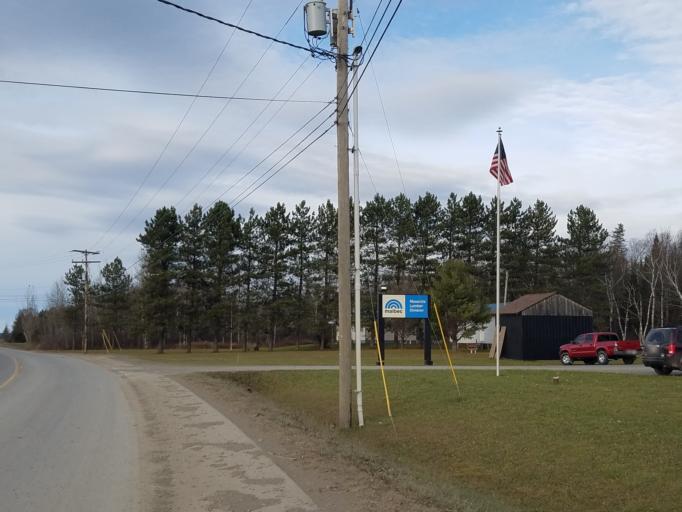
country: US
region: Maine
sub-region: Aroostook County
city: Presque Isle
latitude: 46.5323
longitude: -68.3588
